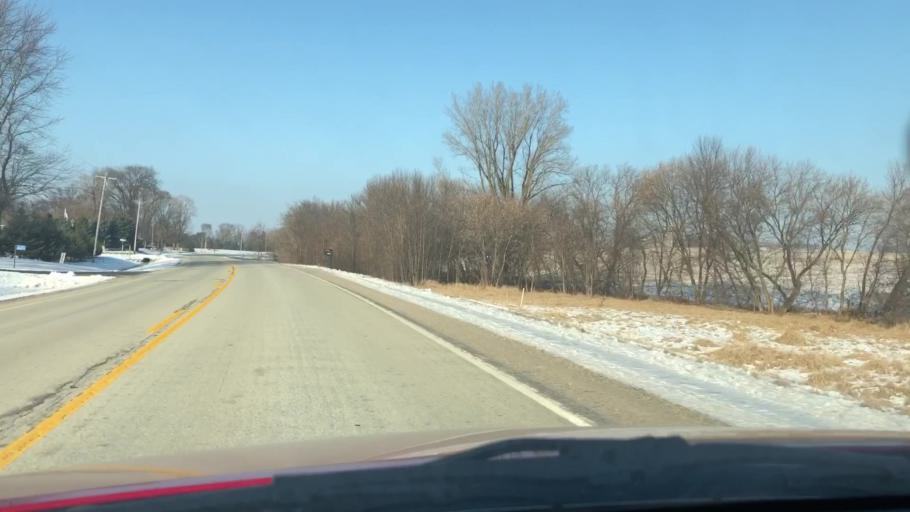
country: US
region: Wisconsin
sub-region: Outagamie County
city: Black Creek
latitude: 44.3931
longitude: -88.3746
